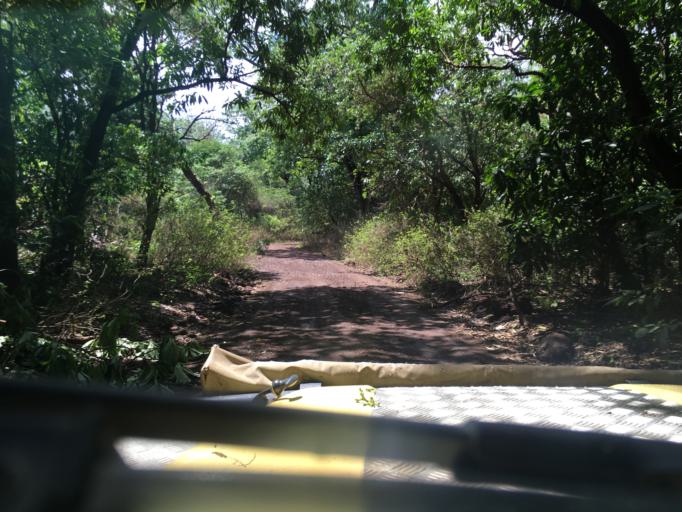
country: TZ
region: Arusha
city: Mto wa Mbu
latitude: -3.4110
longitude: 35.8199
